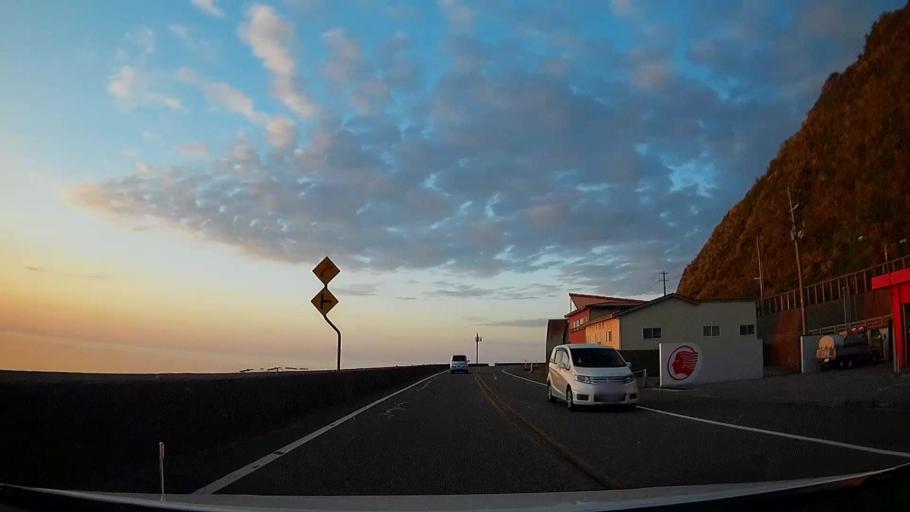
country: JP
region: Niigata
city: Joetsu
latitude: 37.1415
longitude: 138.0597
